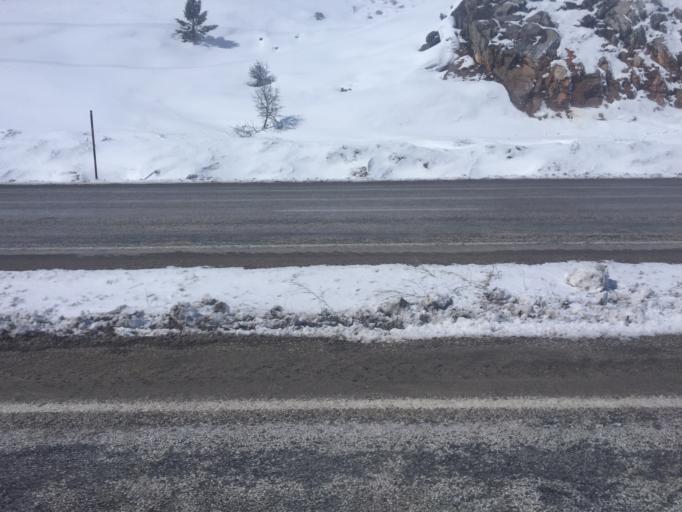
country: TR
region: Kahramanmaras
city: Goksun
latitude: 38.1907
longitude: 36.4569
